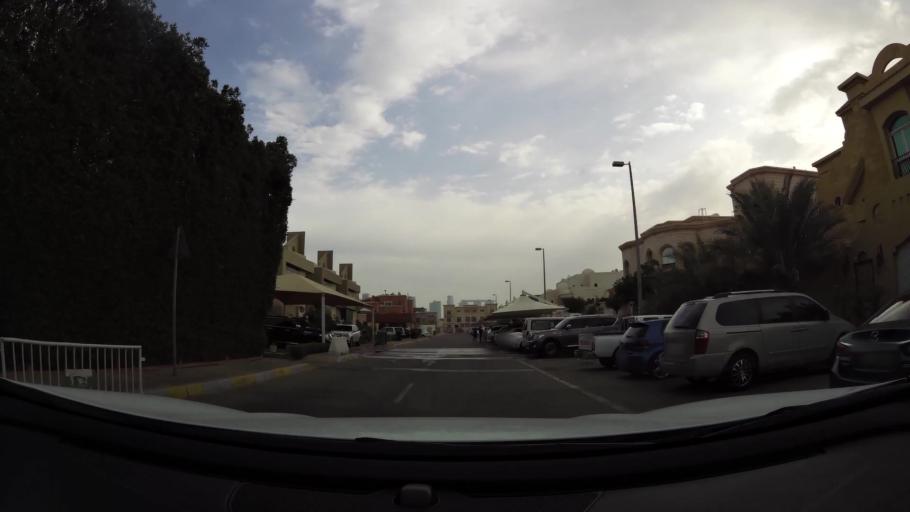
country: AE
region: Abu Dhabi
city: Abu Dhabi
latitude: 24.4736
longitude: 54.3810
